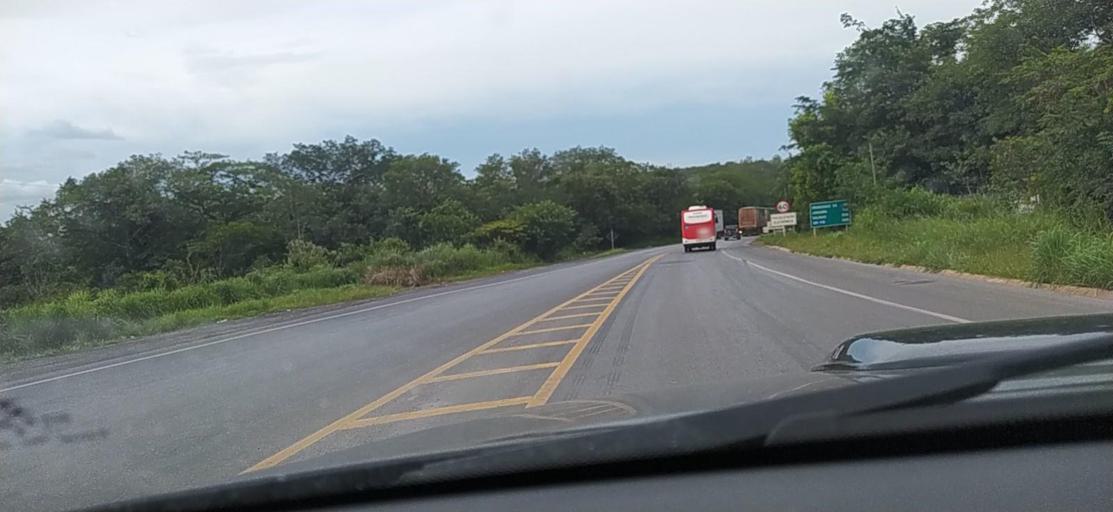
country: BR
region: Minas Gerais
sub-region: Montes Claros
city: Montes Claros
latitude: -16.6748
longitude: -43.7982
